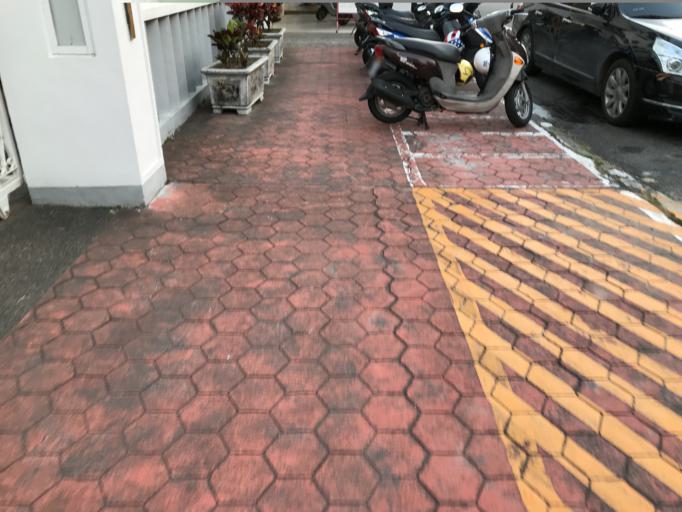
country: TW
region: Taiwan
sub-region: Tainan
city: Tainan
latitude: 22.9934
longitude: 120.2054
